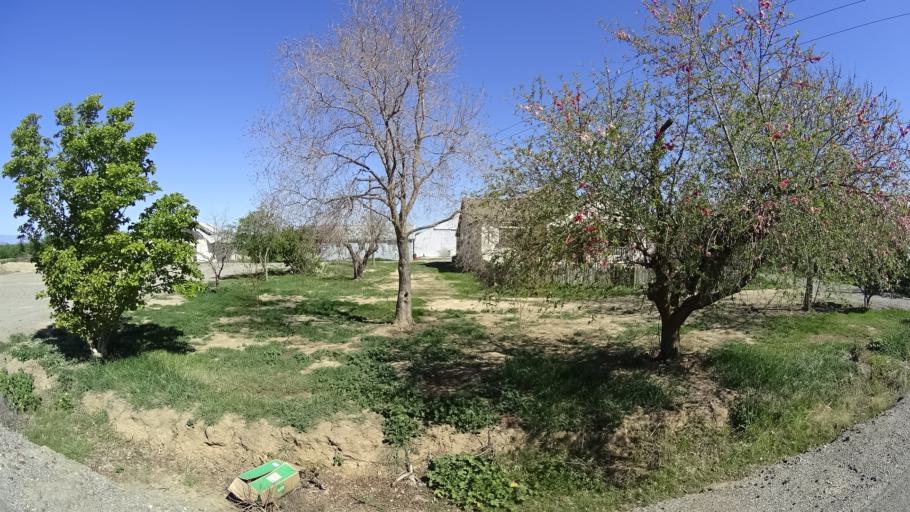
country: US
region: California
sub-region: Glenn County
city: Orland
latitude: 39.6971
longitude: -122.2109
